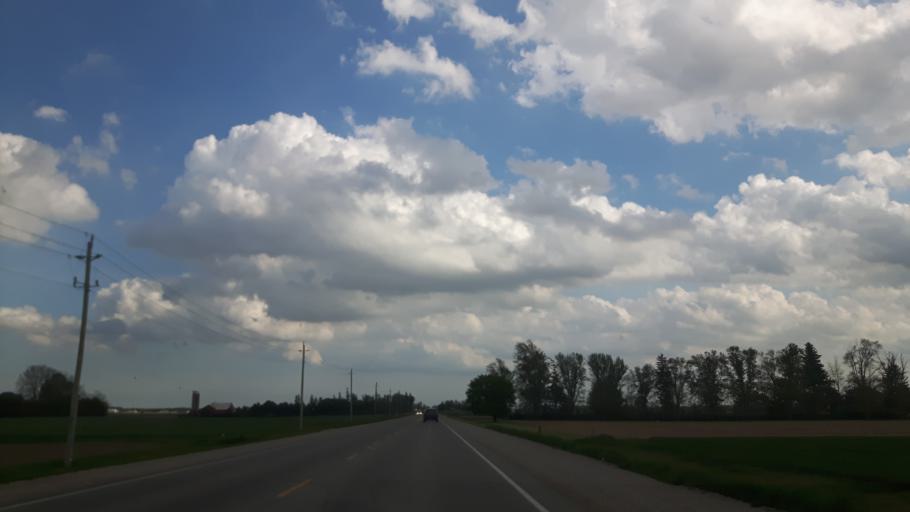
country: CA
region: Ontario
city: South Huron
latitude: 43.3843
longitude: -81.4883
